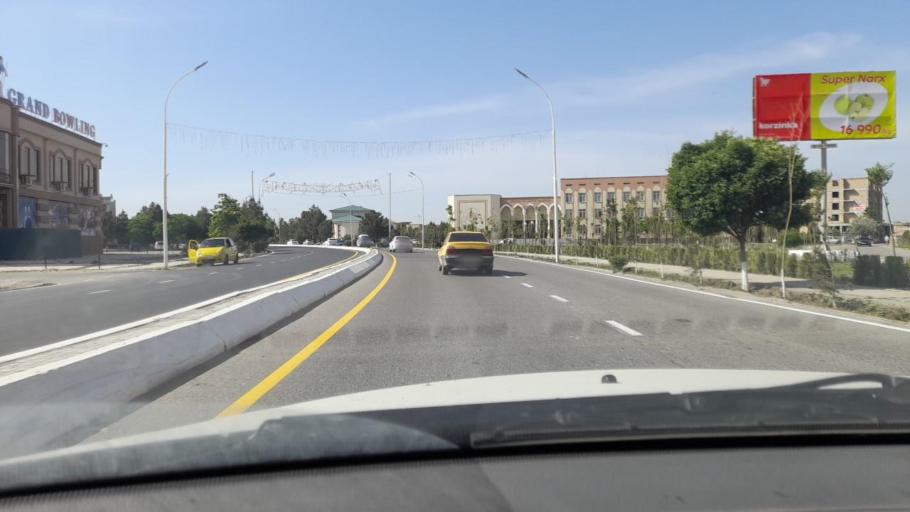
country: UZ
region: Bukhara
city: Bukhara
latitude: 39.7855
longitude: 64.4295
